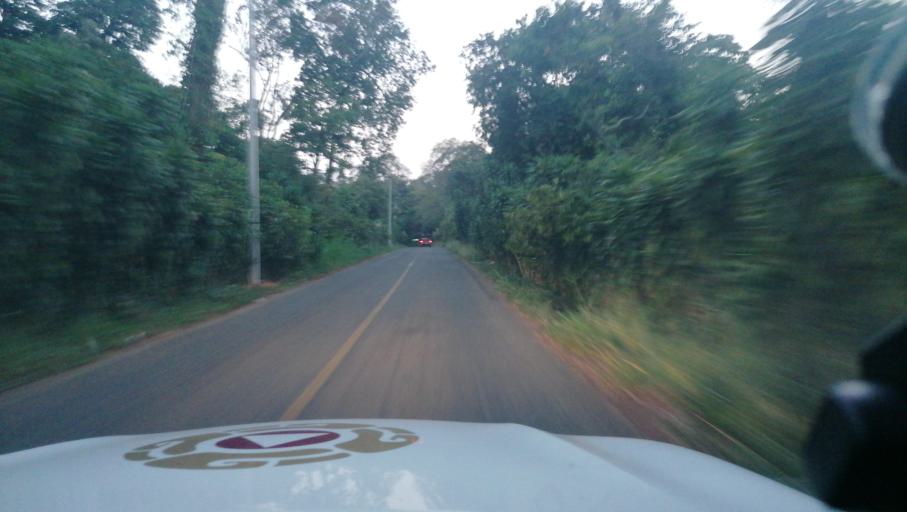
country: MX
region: Chiapas
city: Veinte de Noviembre
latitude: 15.0097
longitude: -92.2464
